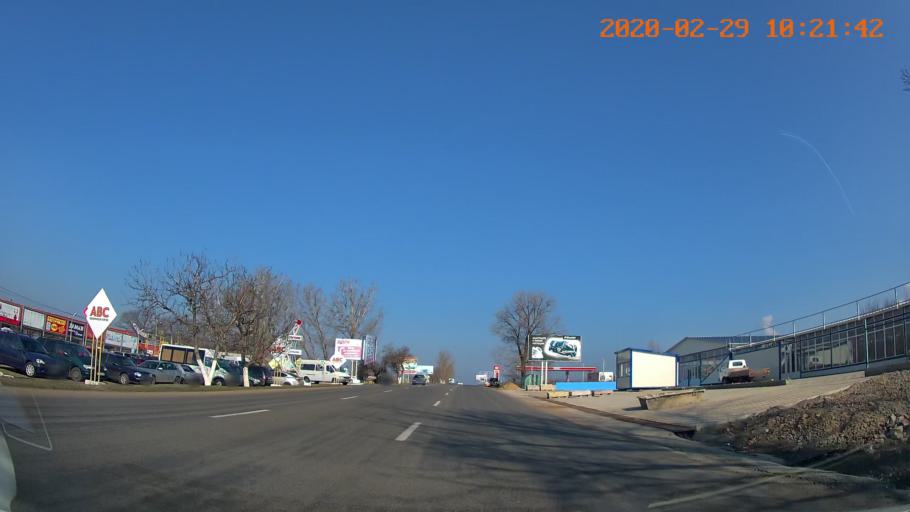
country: MD
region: Telenesti
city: Tiraspolul Nou
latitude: 46.8687
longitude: 29.6088
